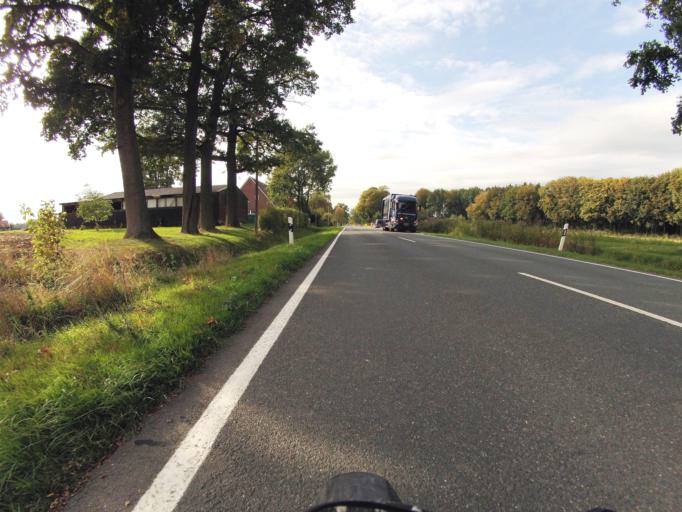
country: DE
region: North Rhine-Westphalia
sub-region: Regierungsbezirk Munster
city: Mettingen
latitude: 52.2808
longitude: 7.8004
